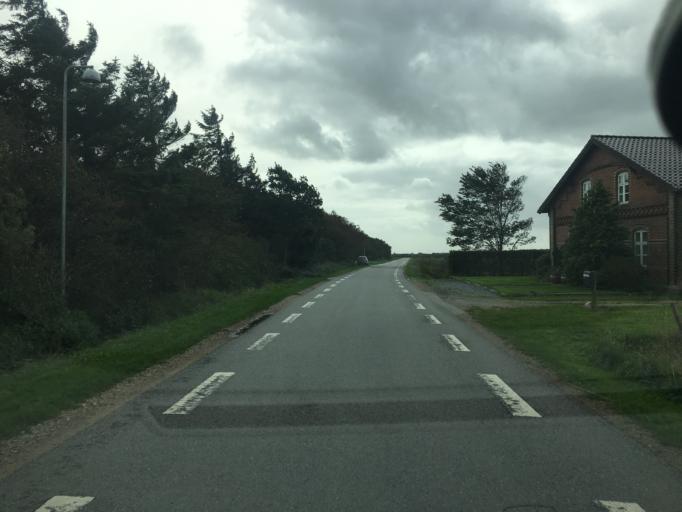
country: DE
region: Schleswig-Holstein
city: Aventoft
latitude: 54.9646
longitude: 8.7666
